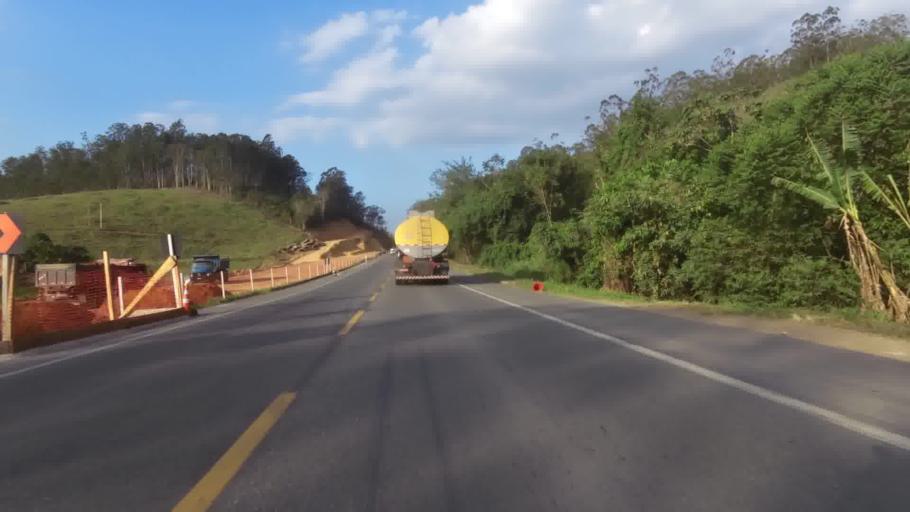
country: BR
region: Espirito Santo
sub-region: Rio Novo Do Sul
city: Rio Novo do Sul
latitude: -20.8947
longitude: -41.0058
